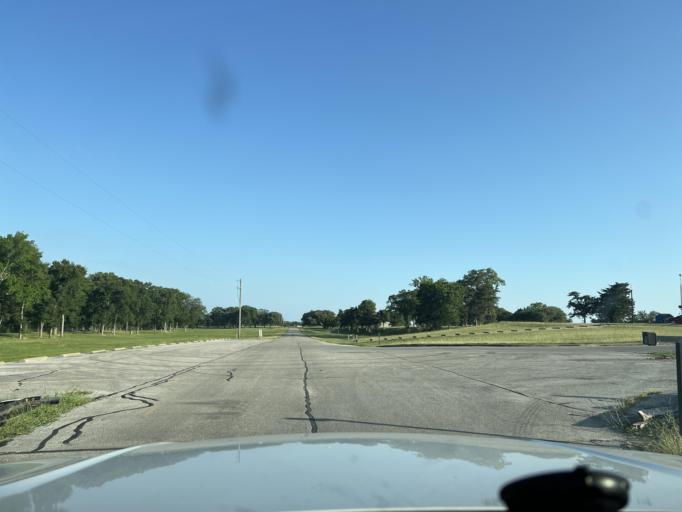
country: US
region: Texas
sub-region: Washington County
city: Brenham
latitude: 30.2172
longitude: -96.3717
